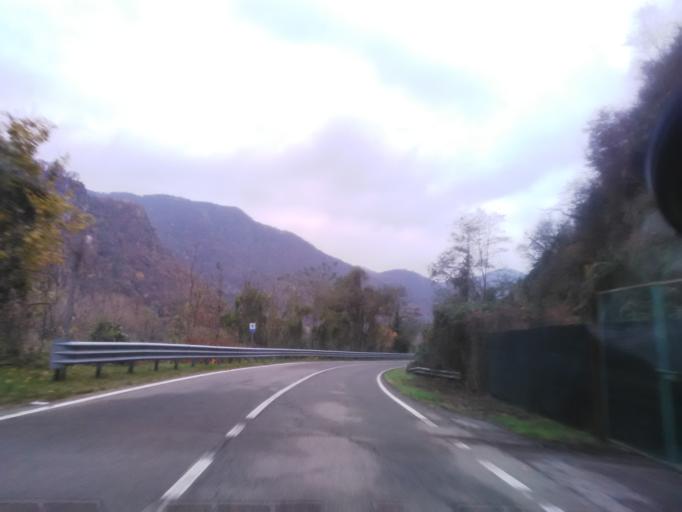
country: IT
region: Piedmont
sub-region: Provincia di Vercelli
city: Varallo
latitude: 45.7993
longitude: 8.2631
